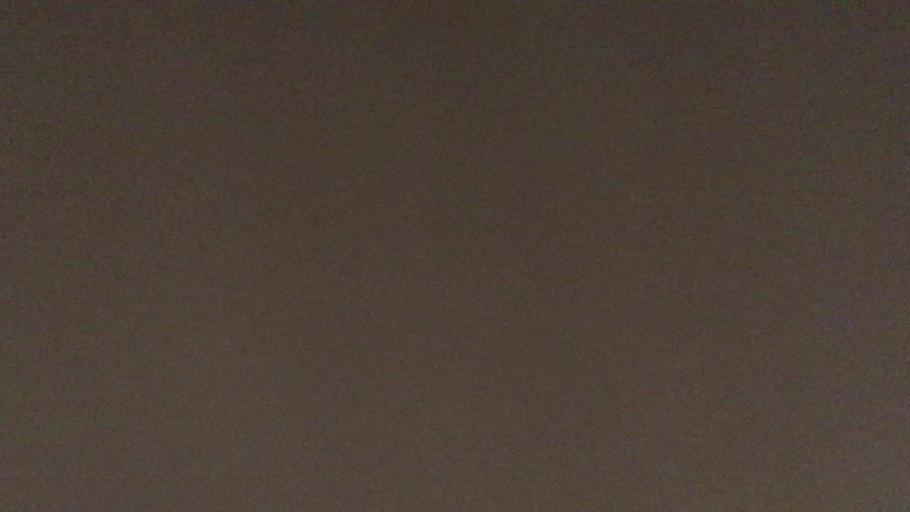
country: US
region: New York
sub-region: Nassau County
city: Jericho
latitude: 40.7998
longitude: -73.5154
